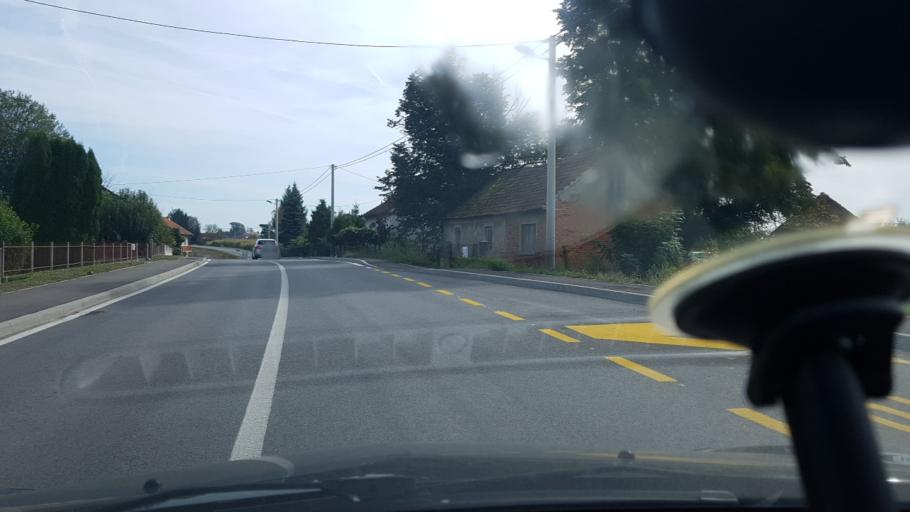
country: HR
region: Krapinsko-Zagorska
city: Marija Bistrica
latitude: 46.0527
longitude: 16.1340
